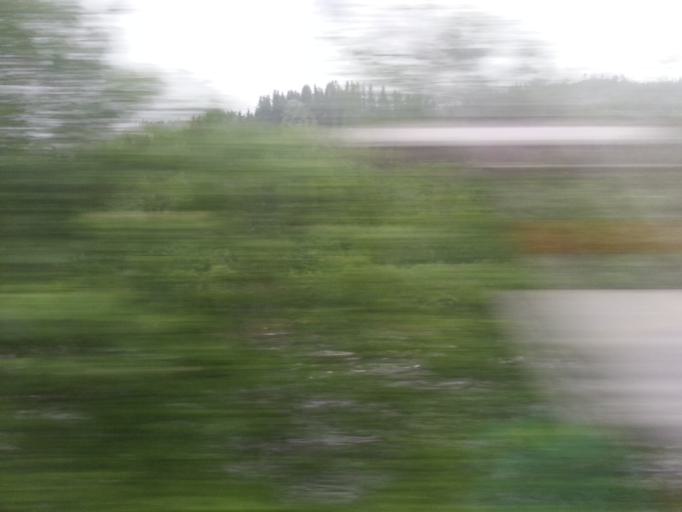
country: NO
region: Sor-Trondelag
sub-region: Midtre Gauldal
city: Storen
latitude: 63.0602
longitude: 10.2879
